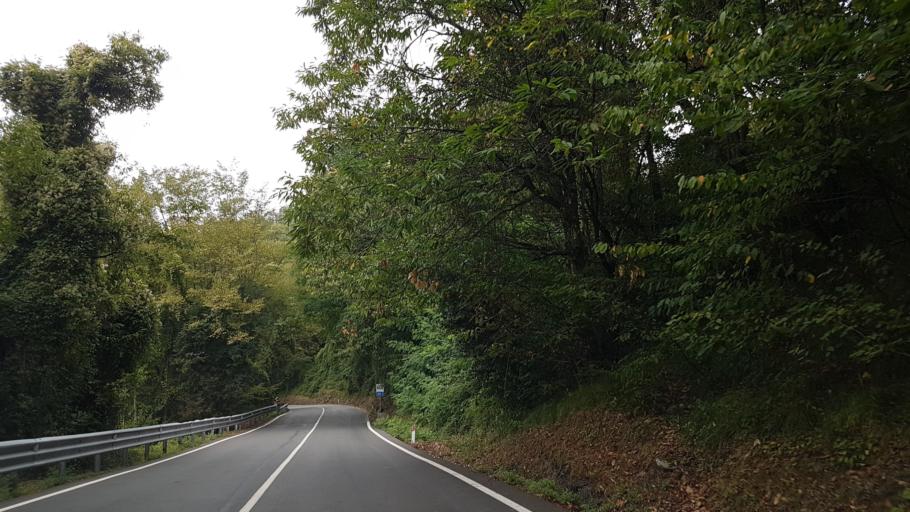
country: IT
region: Liguria
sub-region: Provincia di Genova
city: Castiglione
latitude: 44.2525
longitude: 9.5291
